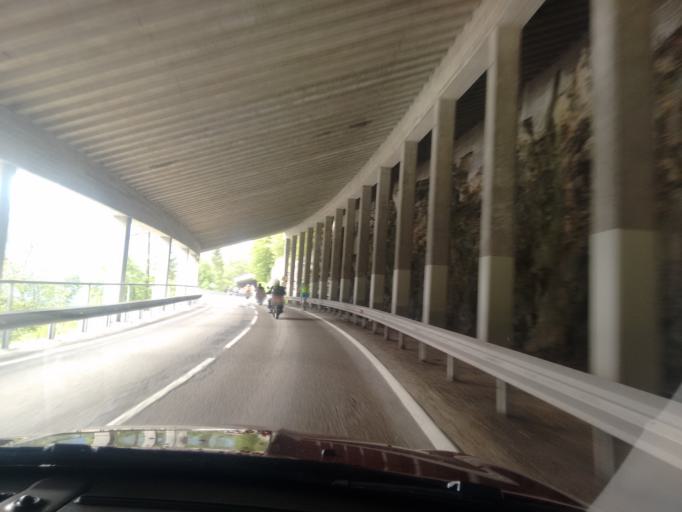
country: AT
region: Upper Austria
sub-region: Politischer Bezirk Gmunden
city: Bad Goisern
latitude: 47.5714
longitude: 13.6496
